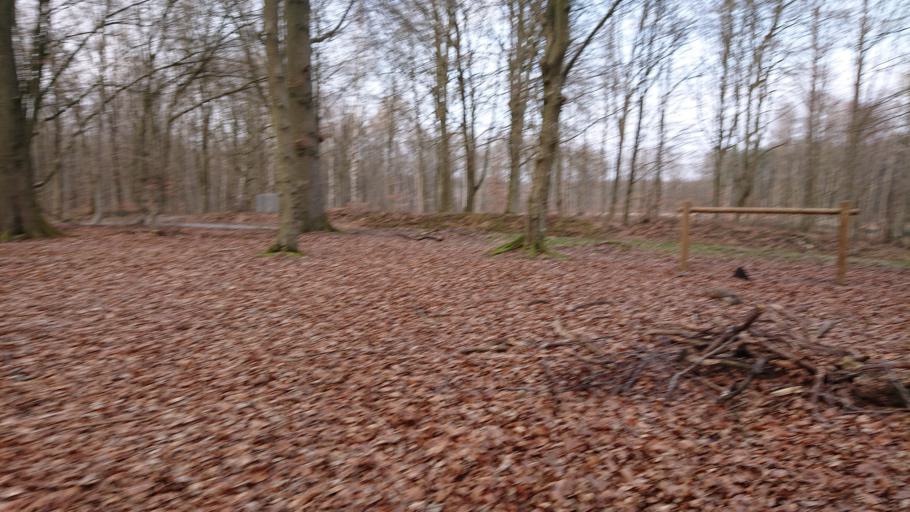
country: FR
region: Nord-Pas-de-Calais
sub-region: Departement du Nord
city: Landrecies
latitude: 50.1676
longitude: 3.7014
